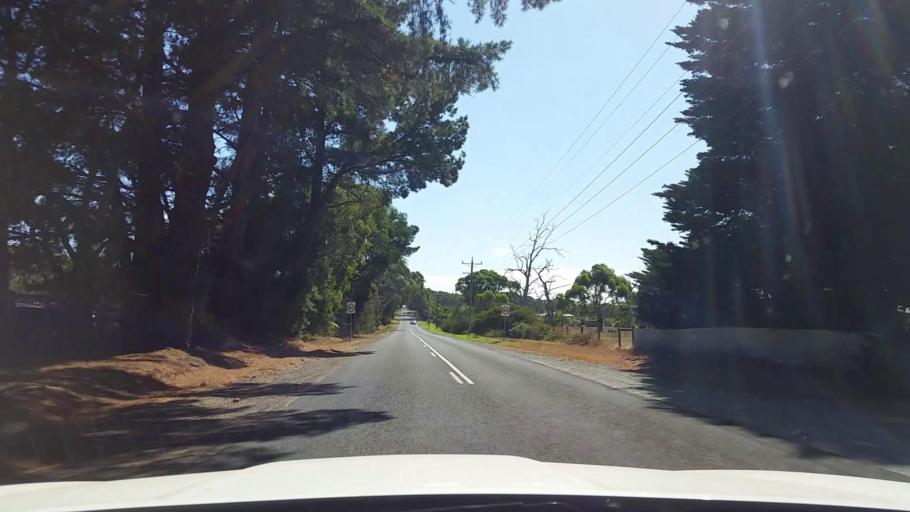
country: AU
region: Victoria
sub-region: Mornington Peninsula
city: Balnarring
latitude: -38.3346
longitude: 145.1457
